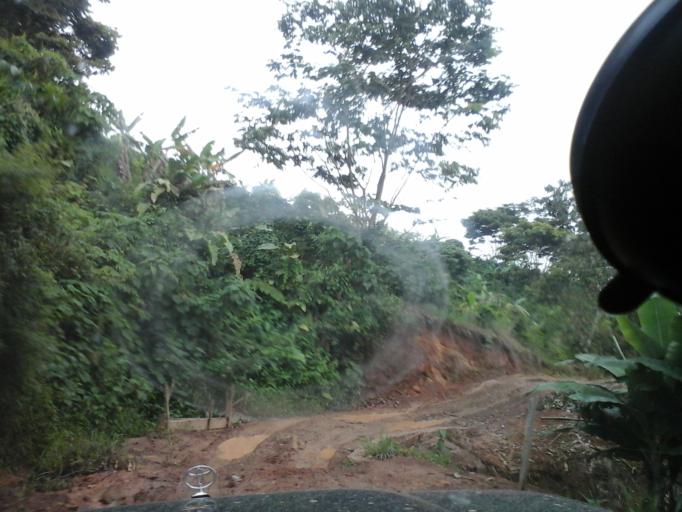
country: CO
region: Cesar
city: Agustin Codazzi
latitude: 9.9614
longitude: -73.0611
